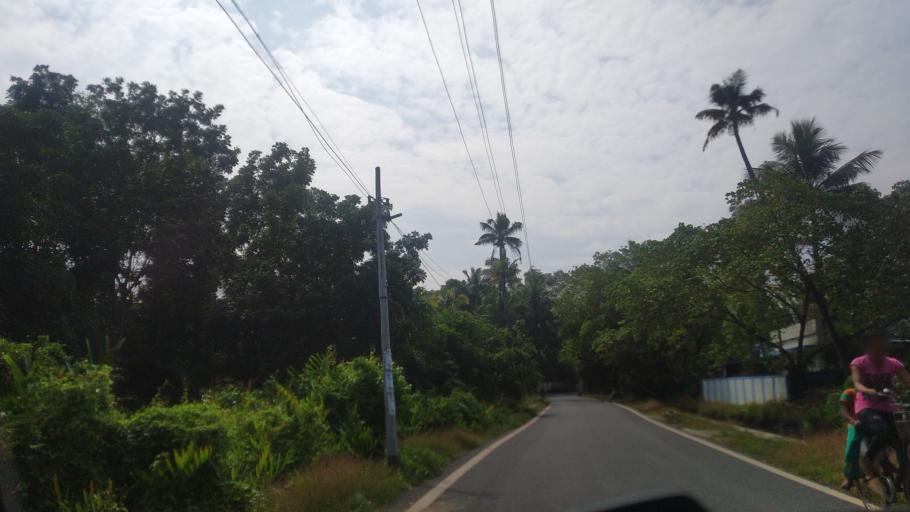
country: IN
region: Kerala
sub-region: Ernakulam
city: Elur
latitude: 10.0799
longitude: 76.2145
